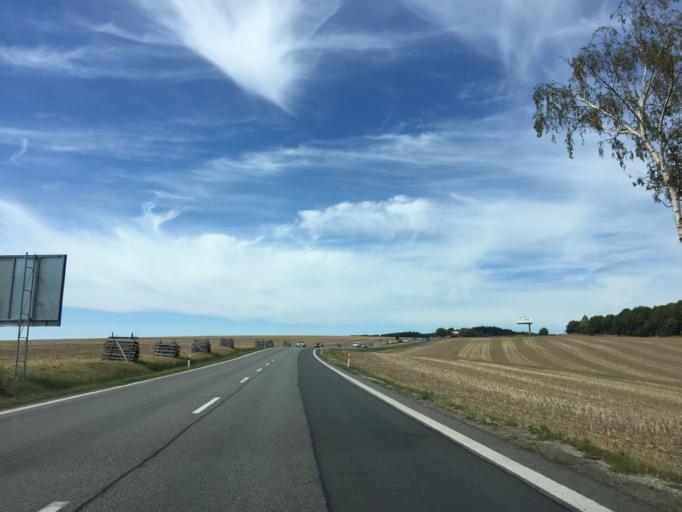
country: CZ
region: Jihocesky
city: Chotoviny
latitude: 49.5581
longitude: 14.6637
